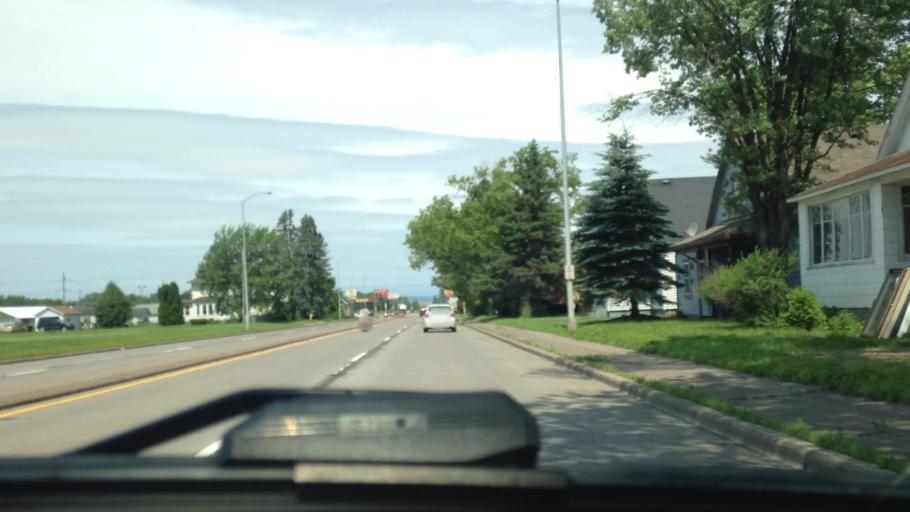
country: US
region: Wisconsin
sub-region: Douglas County
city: Superior
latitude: 46.6760
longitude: -92.0082
